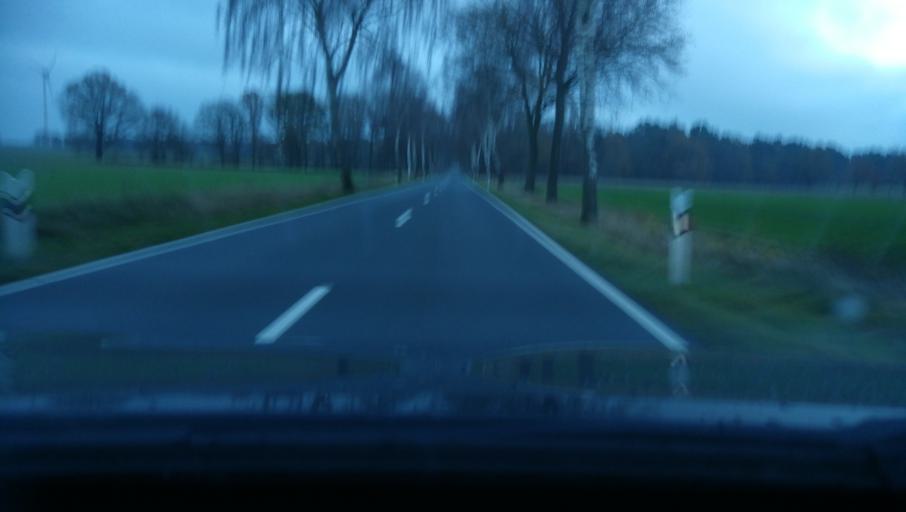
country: DE
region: Lower Saxony
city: Fintel
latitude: 53.1372
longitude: 9.7030
